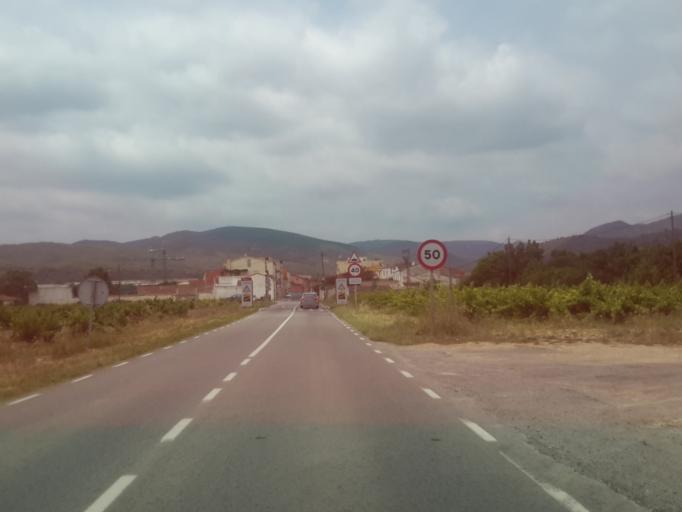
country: ES
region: Catalonia
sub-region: Provincia de Barcelona
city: Sant Marti Sarroca
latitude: 41.3837
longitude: 1.5891
